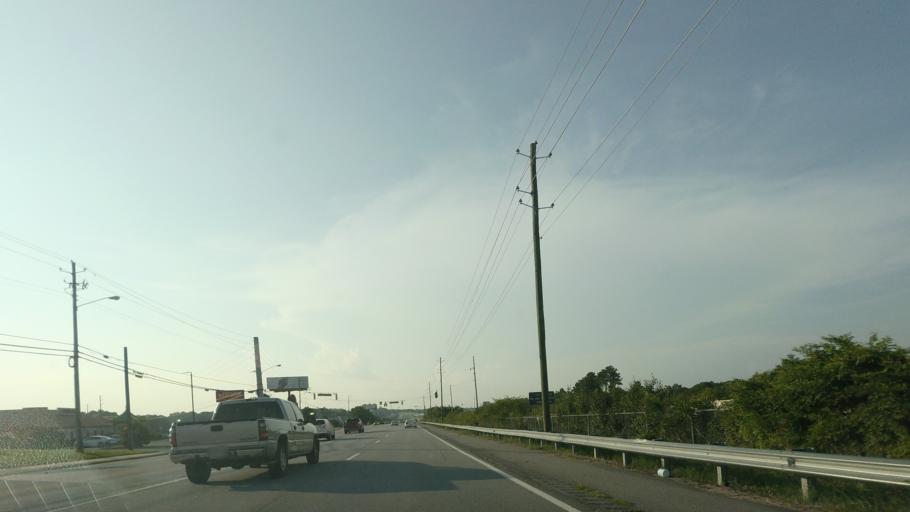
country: US
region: Georgia
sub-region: Bibb County
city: Macon
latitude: 32.8904
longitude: -83.6766
